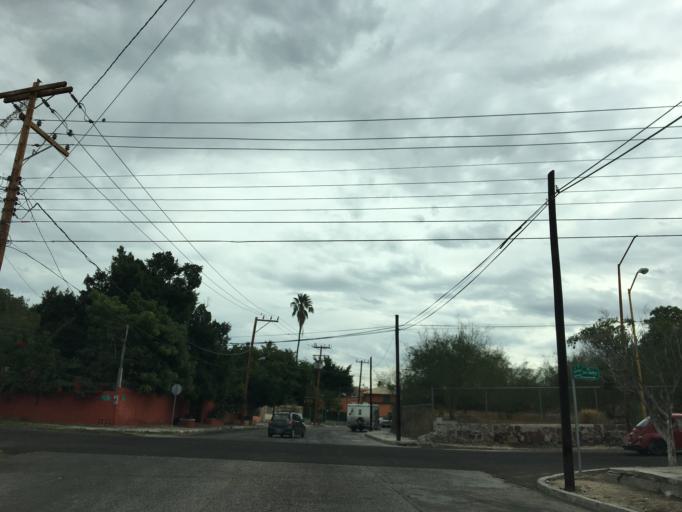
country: MX
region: Baja California Sur
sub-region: La Paz
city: La Paz
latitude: 24.1574
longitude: -110.3187
